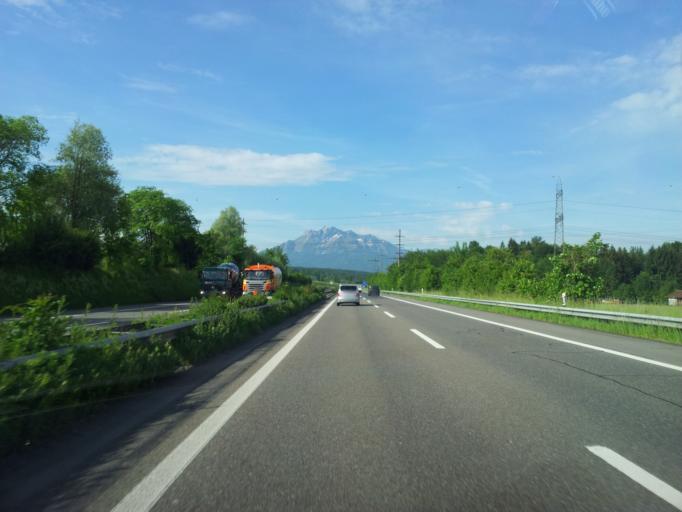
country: CH
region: Lucerne
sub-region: Lucerne-Land District
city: Buchrain
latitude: 47.1097
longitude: 8.3512
